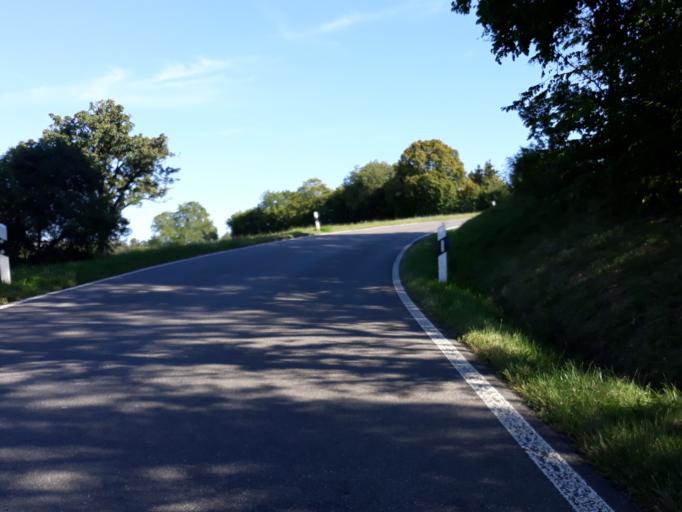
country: DE
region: Baden-Wuerttemberg
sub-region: Karlsruhe Region
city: Ostelsheim
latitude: 48.7215
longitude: 8.8517
